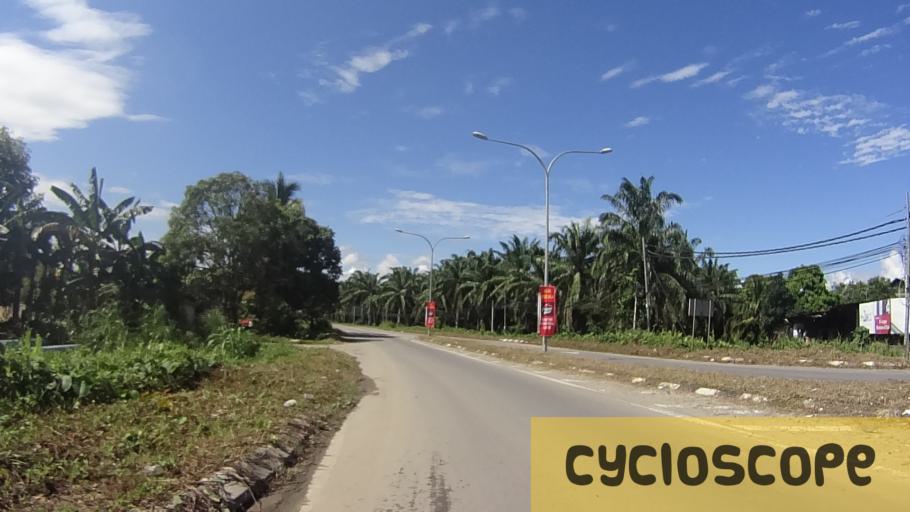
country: MY
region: Sabah
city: Beaufort
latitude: 5.3414
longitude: 115.7250
